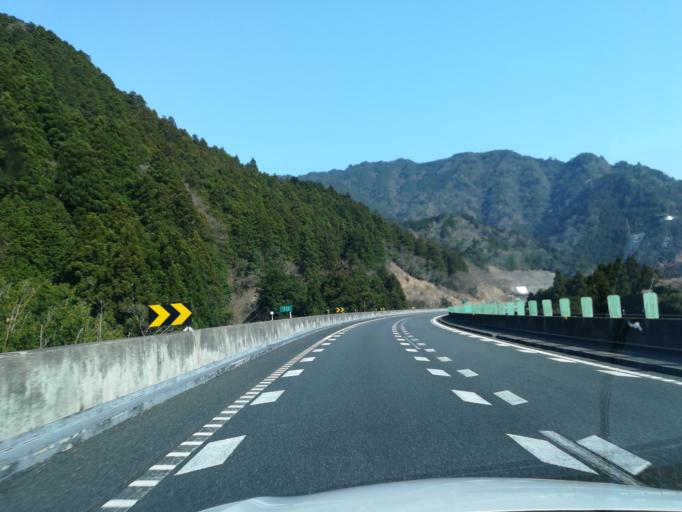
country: JP
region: Ehime
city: Kawanoecho
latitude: 33.9070
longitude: 133.6301
